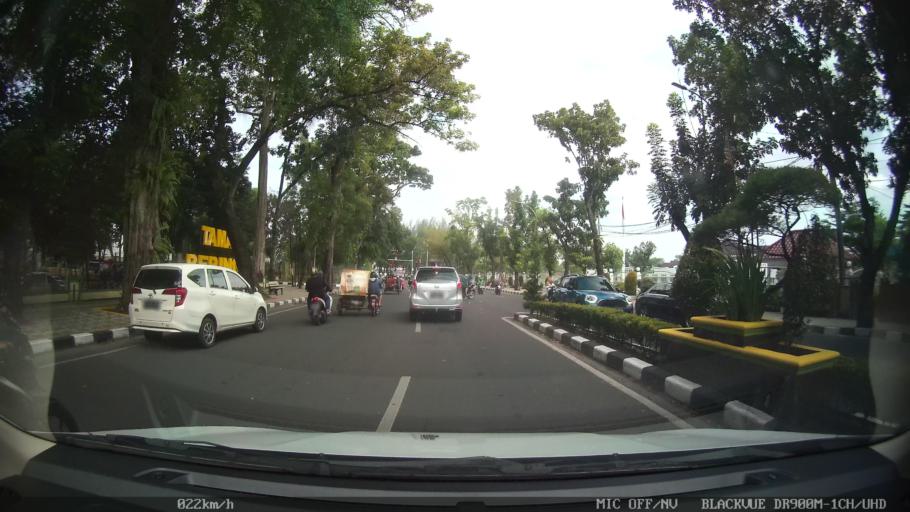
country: ID
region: North Sumatra
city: Medan
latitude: 3.5757
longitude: 98.6693
